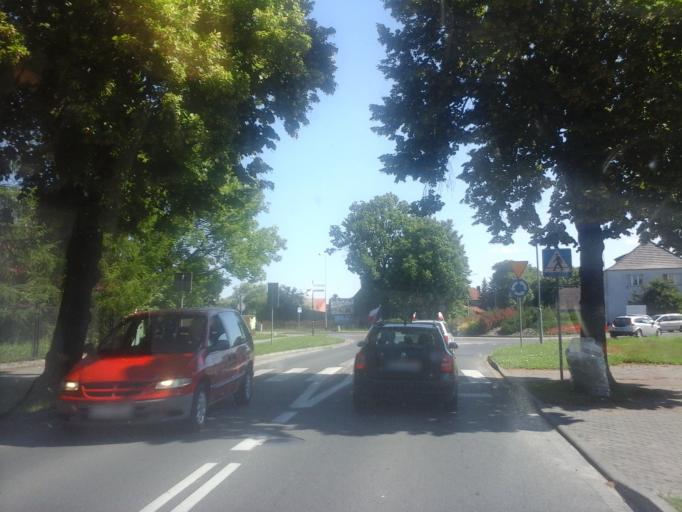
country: PL
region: West Pomeranian Voivodeship
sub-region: Powiat bialogardzki
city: Bialogard
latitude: 54.0073
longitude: 15.9968
